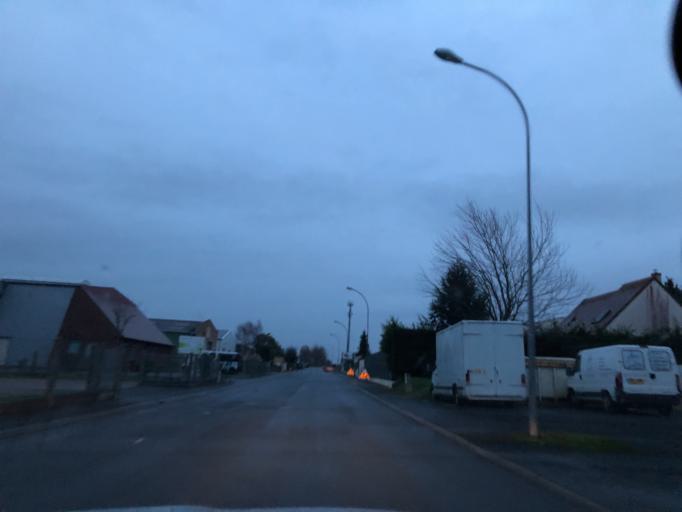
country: FR
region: Lower Normandy
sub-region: Departement du Calvados
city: Douvres-la-Delivrande
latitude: 49.2865
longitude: -0.3746
